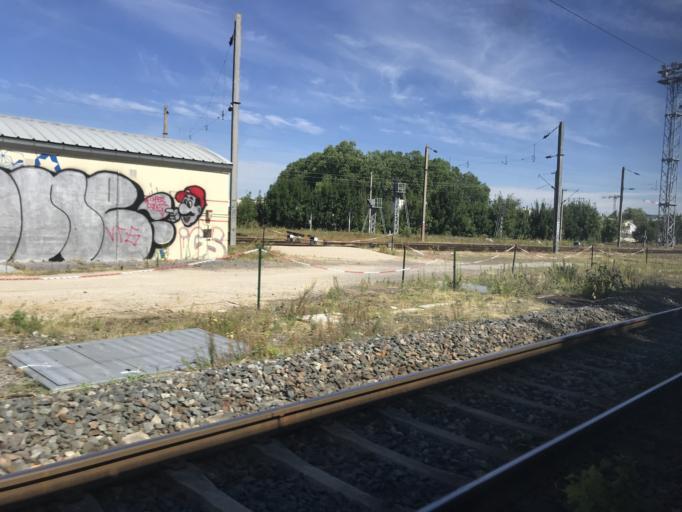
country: FR
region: Champagne-Ardenne
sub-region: Departement de la Marne
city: Reims
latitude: 49.2554
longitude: 4.0191
